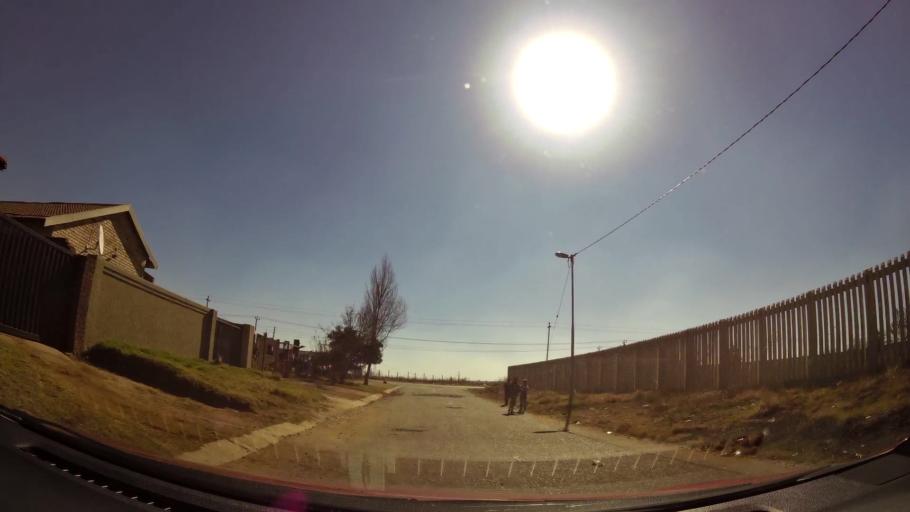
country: ZA
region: Gauteng
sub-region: City of Johannesburg Metropolitan Municipality
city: Soweto
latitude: -26.2158
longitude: 27.8258
